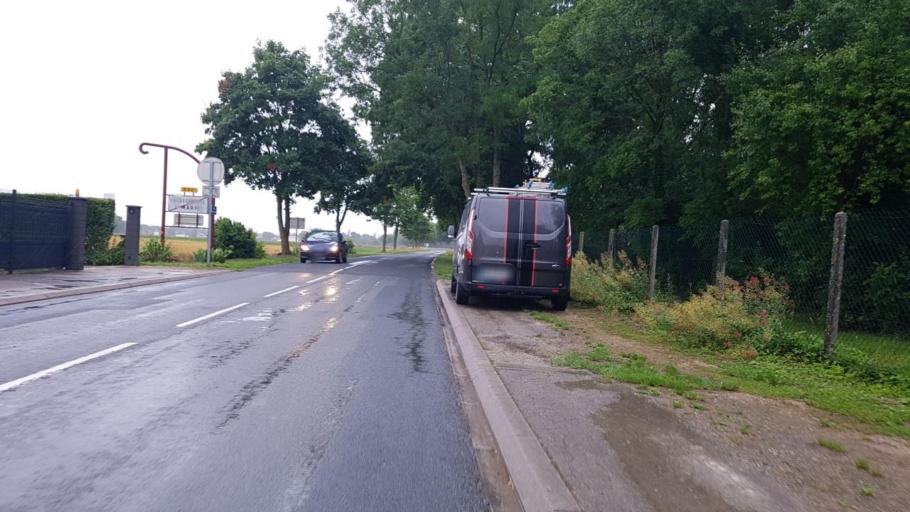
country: FR
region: Champagne-Ardenne
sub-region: Departement de la Marne
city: Sarry
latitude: 48.8742
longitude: 4.4581
